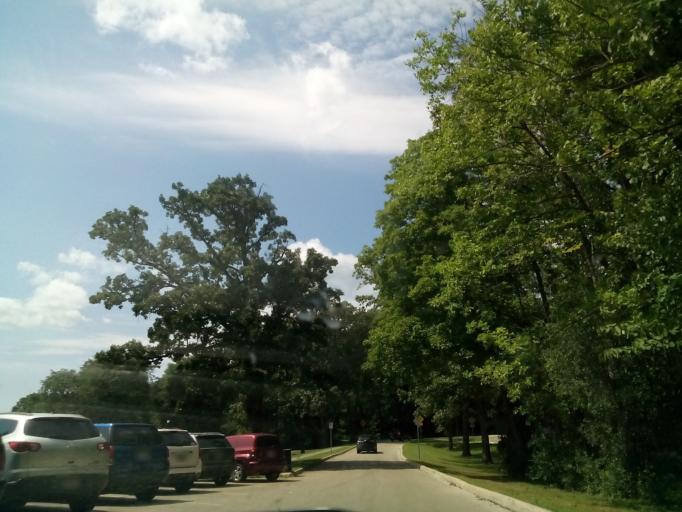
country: US
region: Wisconsin
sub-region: Dane County
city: Madison
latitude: 43.0616
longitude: -89.4110
